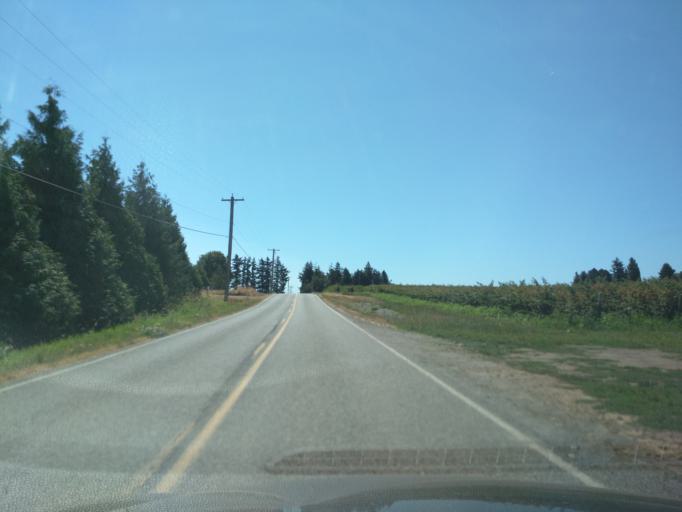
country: US
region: Washington
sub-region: Whatcom County
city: Everson
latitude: 48.9133
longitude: -122.3976
